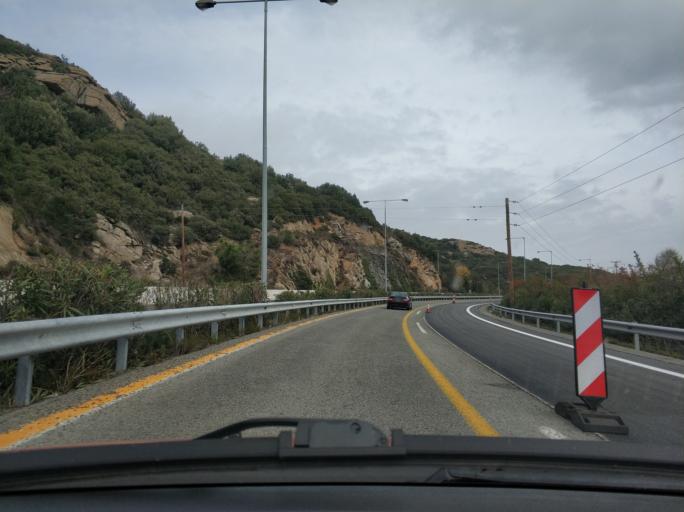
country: GR
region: East Macedonia and Thrace
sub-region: Nomos Kavalas
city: Palaio Tsifliki
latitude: 40.9141
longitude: 24.3599
